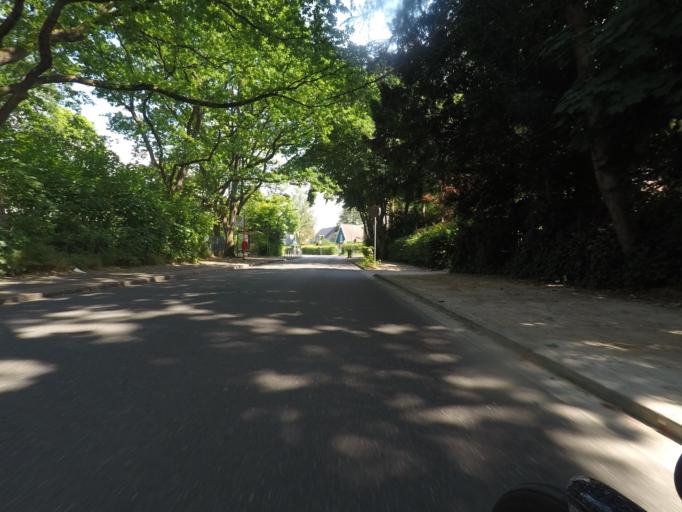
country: DE
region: Hamburg
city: Sasel
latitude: 53.6581
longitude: 10.1000
